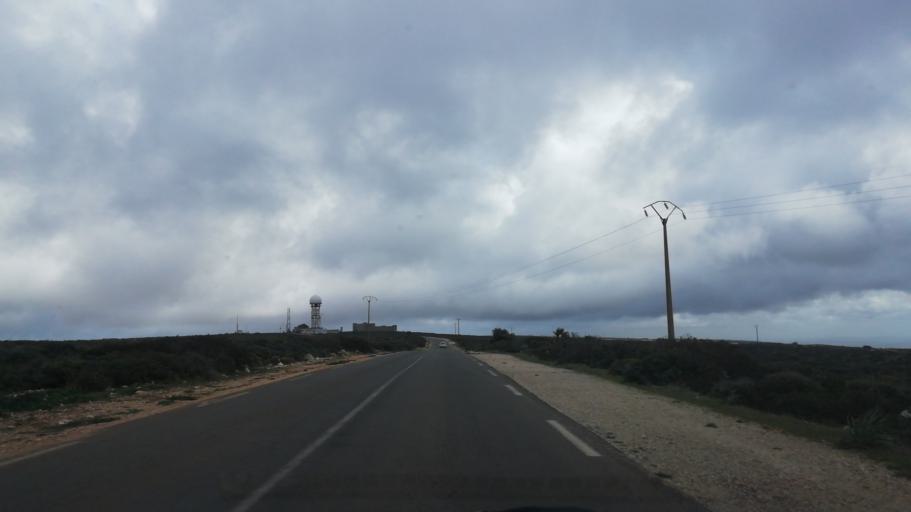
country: DZ
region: Oran
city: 'Ain el Turk
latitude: 35.6923
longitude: -0.7772
